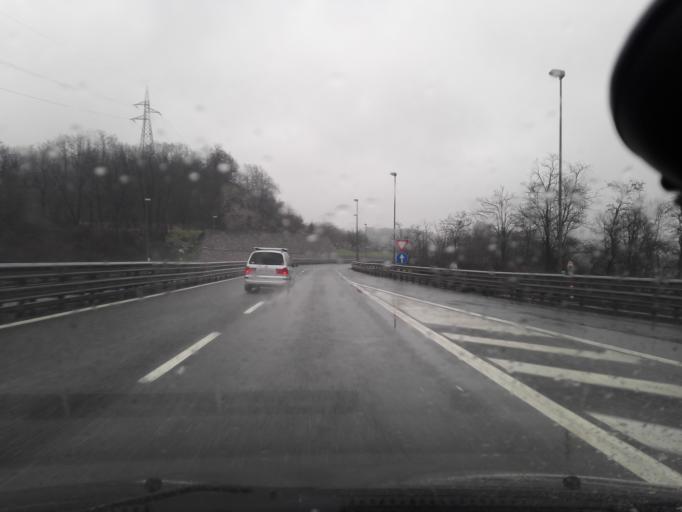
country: IT
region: Piedmont
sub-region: Provincia di Alessandria
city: Vignole Borbera
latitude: 44.7018
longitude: 8.8897
